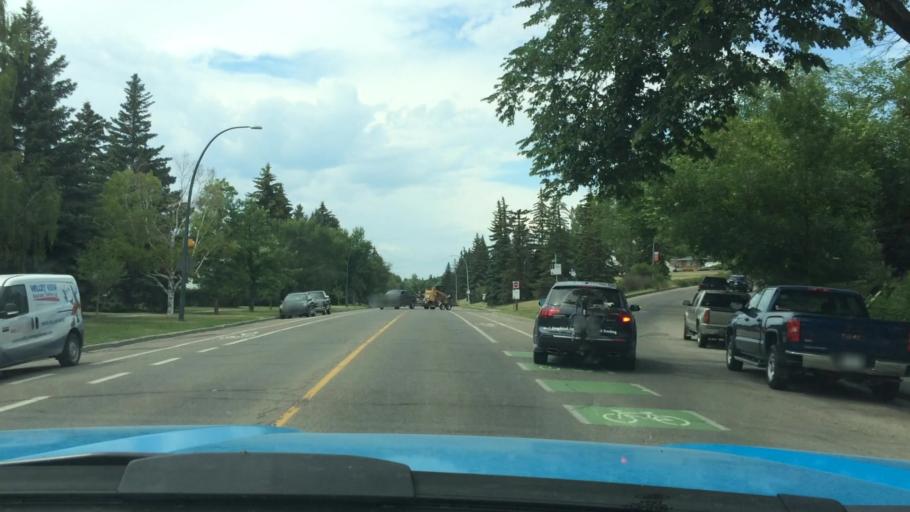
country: CA
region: Alberta
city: Calgary
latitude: 51.0791
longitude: -114.0863
